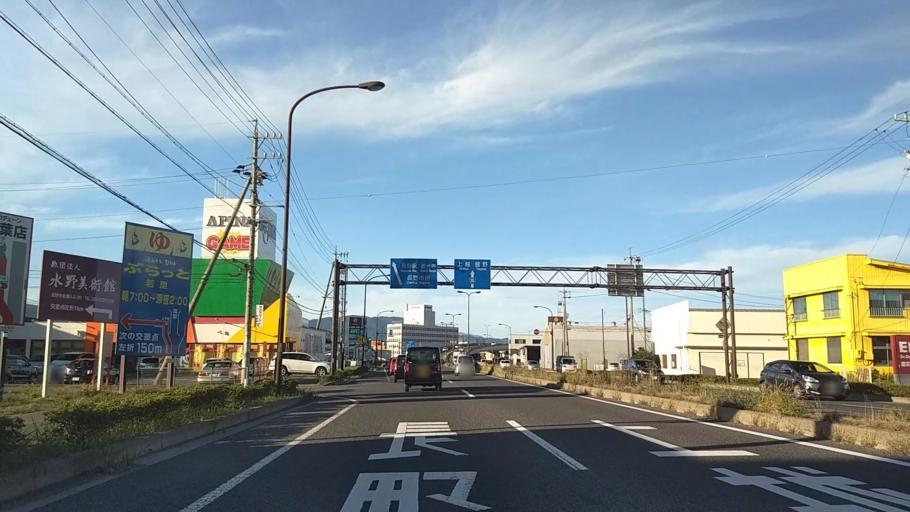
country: JP
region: Nagano
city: Nagano-shi
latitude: 36.6257
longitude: 138.2005
